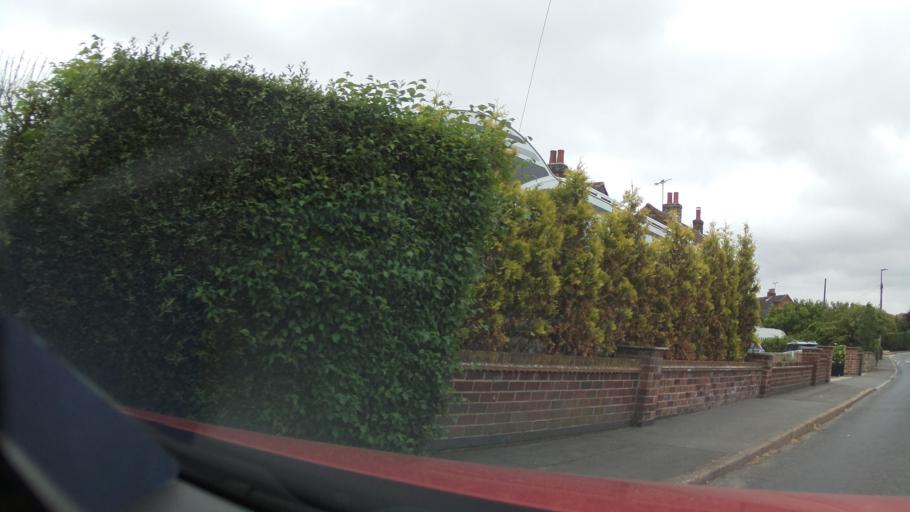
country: GB
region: England
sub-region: Derbyshire
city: Swadlincote
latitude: 52.7883
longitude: -1.5270
